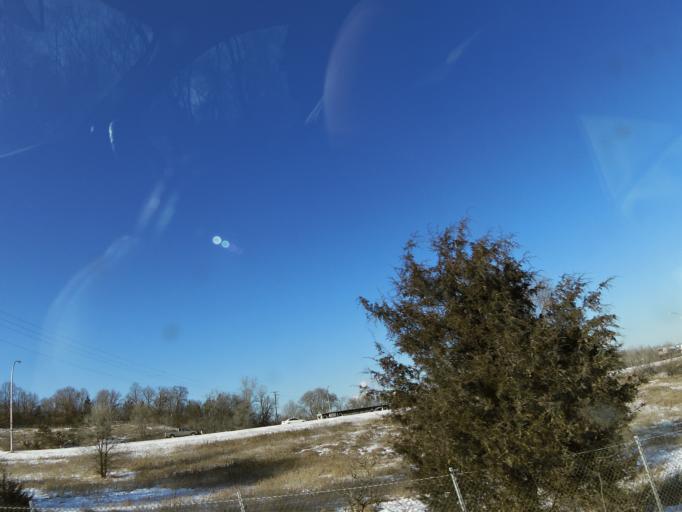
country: US
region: Minnesota
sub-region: Washington County
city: Lakeland
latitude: 44.9594
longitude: -92.7784
